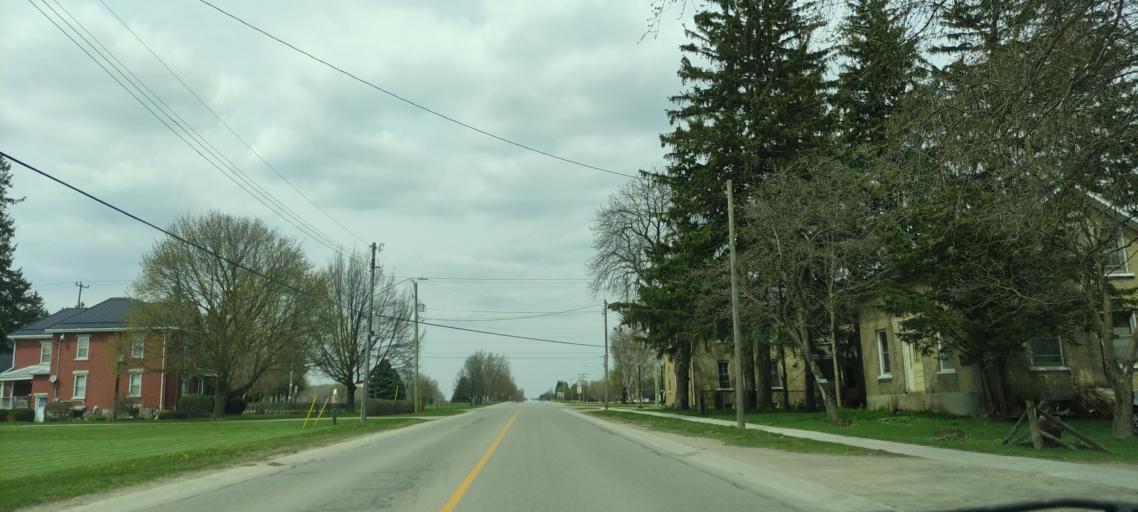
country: CA
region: Ontario
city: Stratford
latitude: 43.3317
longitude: -80.8364
